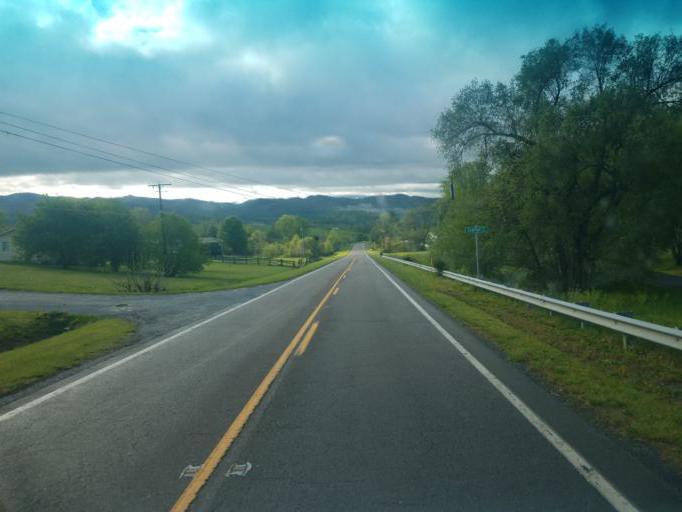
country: US
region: Virginia
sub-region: Washington County
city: Emory
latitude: 36.6794
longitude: -81.8131
